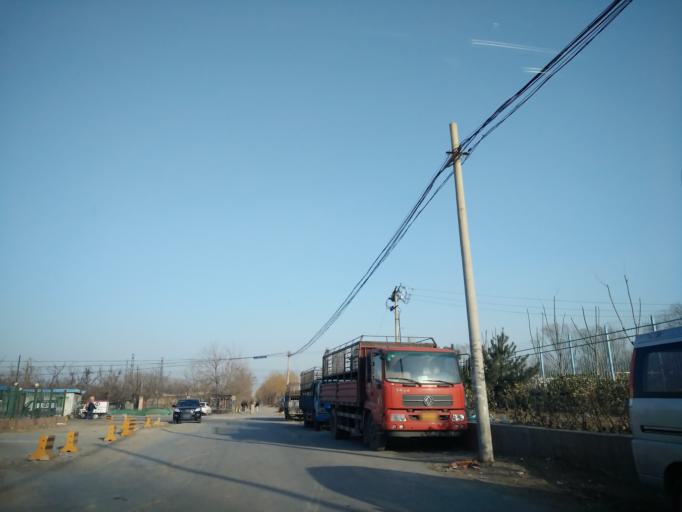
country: CN
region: Beijing
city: Xingfeng
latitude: 39.7215
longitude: 116.3763
